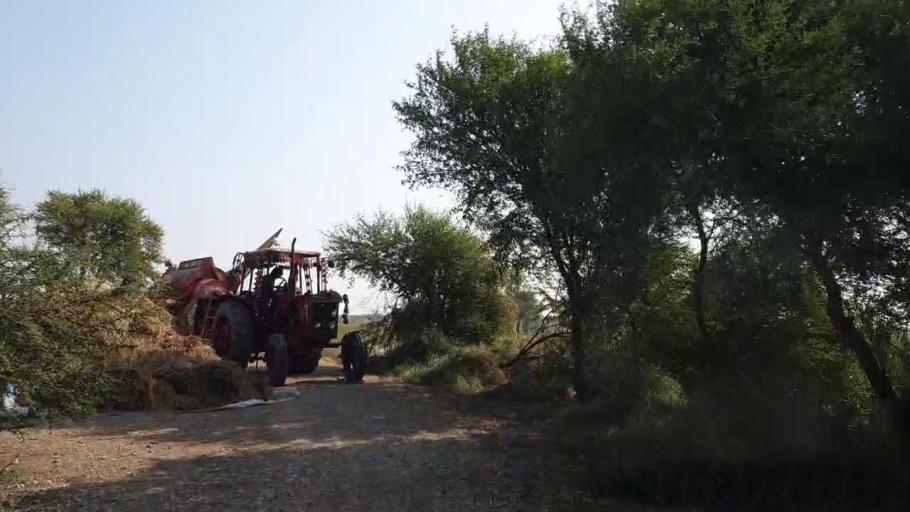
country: PK
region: Sindh
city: Tando Muhammad Khan
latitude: 25.0692
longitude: 68.4239
